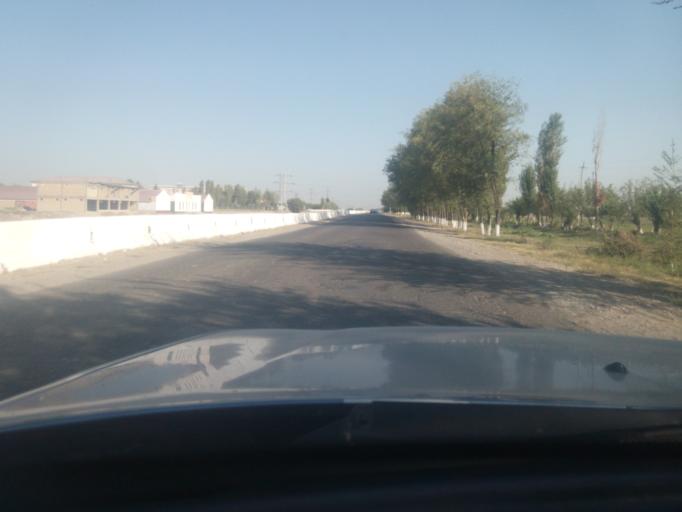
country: UZ
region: Sirdaryo
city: Guliston
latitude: 40.5142
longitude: 68.7943
